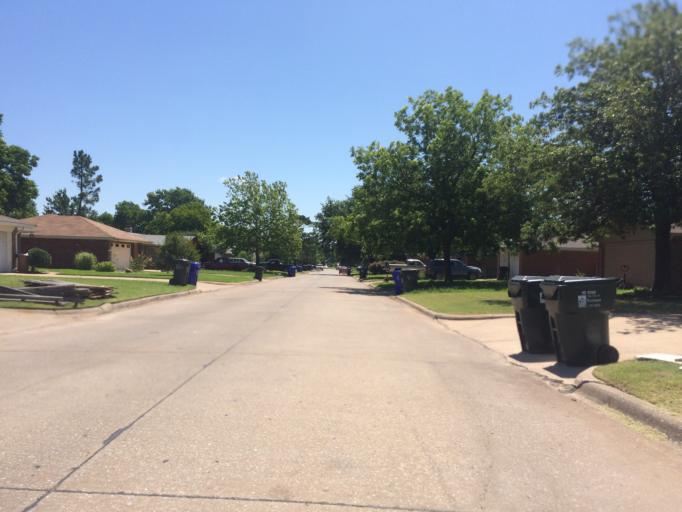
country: US
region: Oklahoma
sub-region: Cleveland County
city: Norman
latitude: 35.2371
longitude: -97.4487
